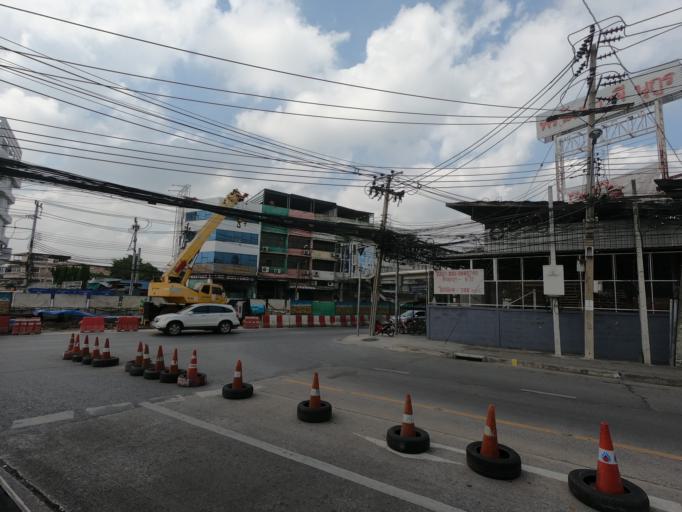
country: TH
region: Bangkok
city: Huai Khwang
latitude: 13.7848
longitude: 100.5857
